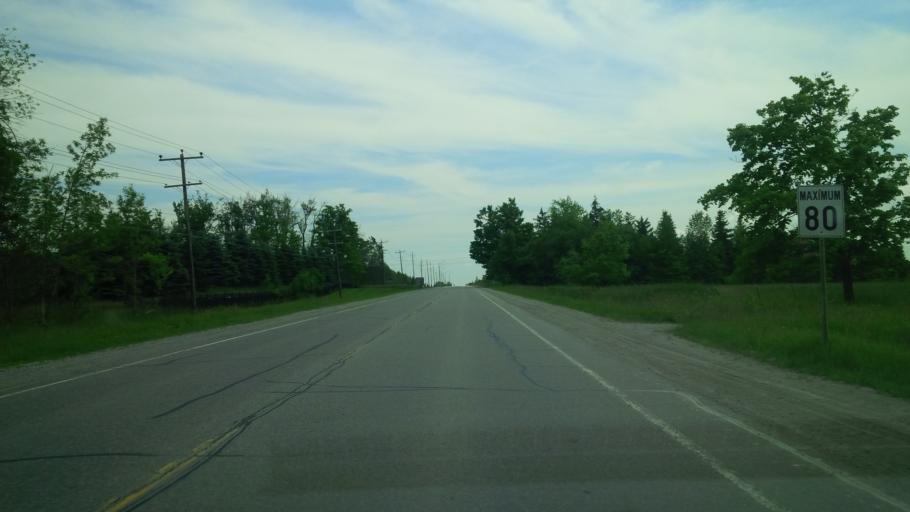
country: CA
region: Ontario
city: Burlington
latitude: 43.4020
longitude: -79.8721
